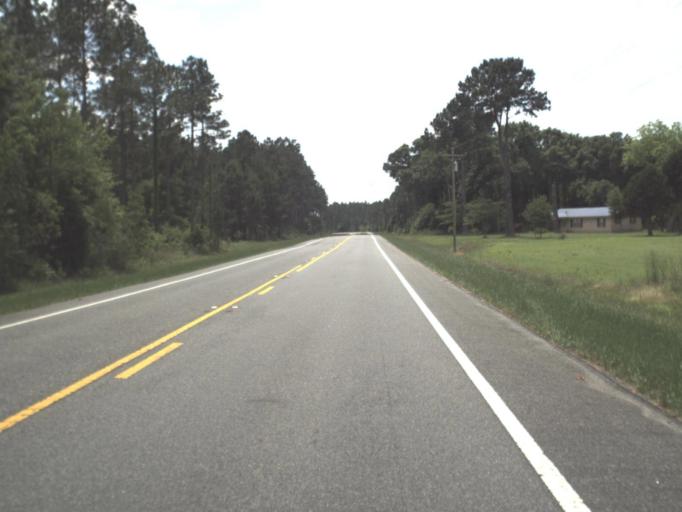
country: US
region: Florida
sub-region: Calhoun County
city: Blountstown
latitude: 30.3507
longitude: -85.1109
